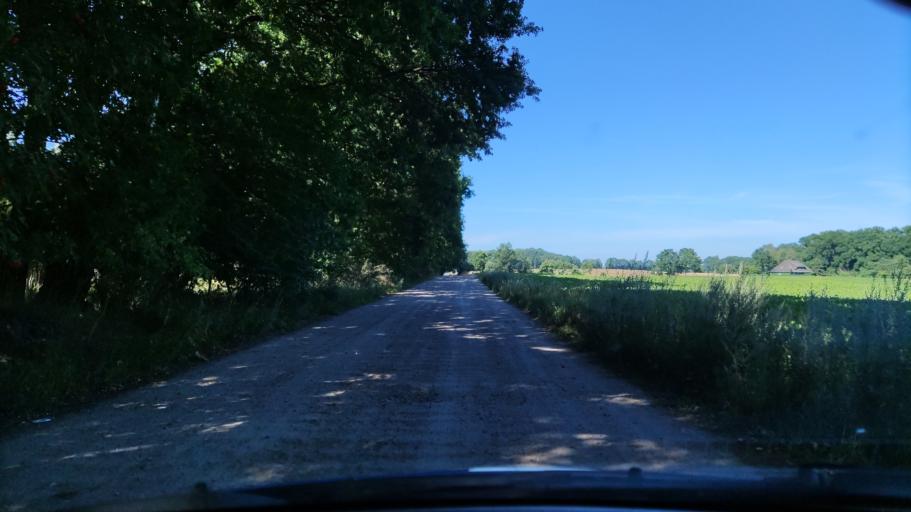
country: DE
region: Lower Saxony
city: Thomasburg
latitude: 53.1837
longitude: 10.6743
